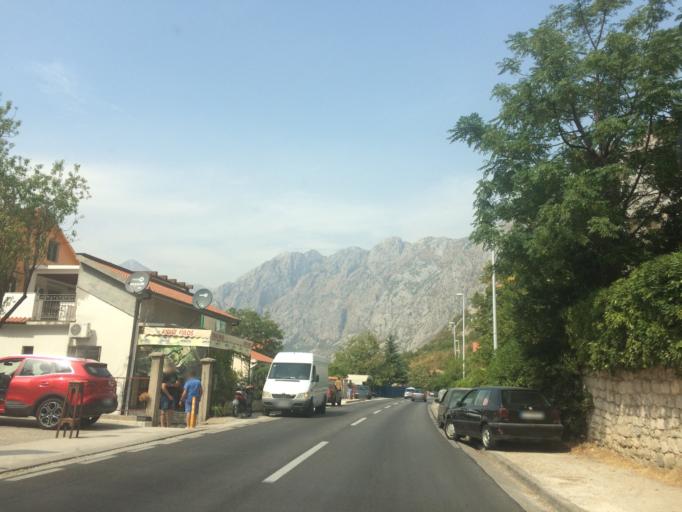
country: ME
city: Dobrota
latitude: 42.4674
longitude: 18.7645
